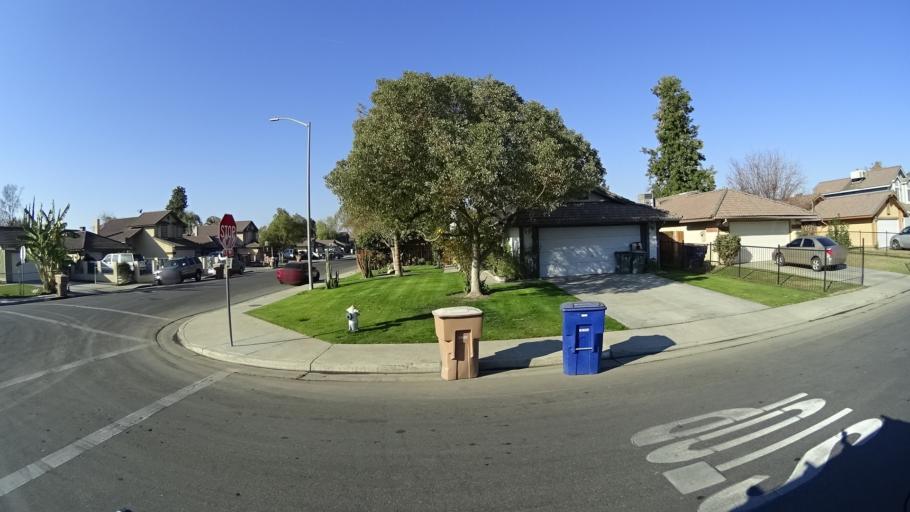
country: US
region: California
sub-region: Kern County
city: Greenfield
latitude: 35.3054
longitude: -119.0173
